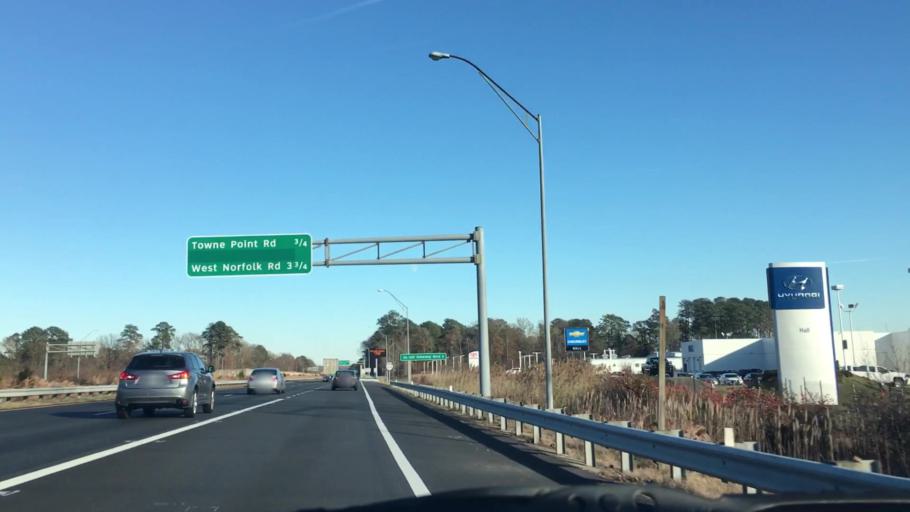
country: US
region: Virginia
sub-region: City of Portsmouth
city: Portsmouth Heights
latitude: 36.8676
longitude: -76.4189
